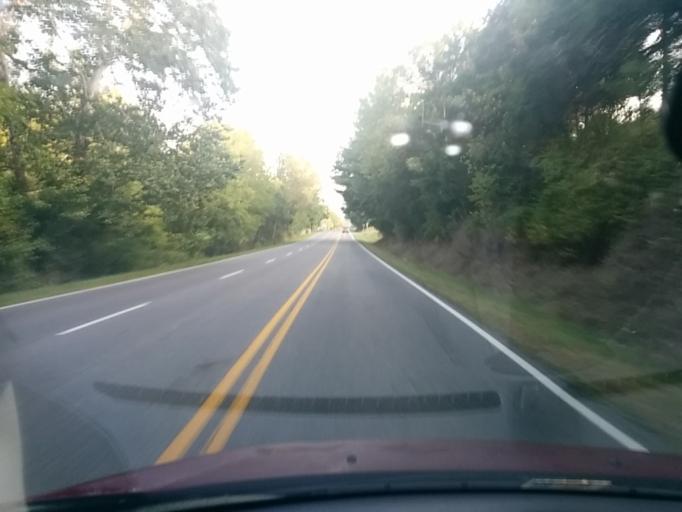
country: US
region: Virginia
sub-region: City of Lexington
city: Lexington
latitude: 37.7658
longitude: -79.4470
